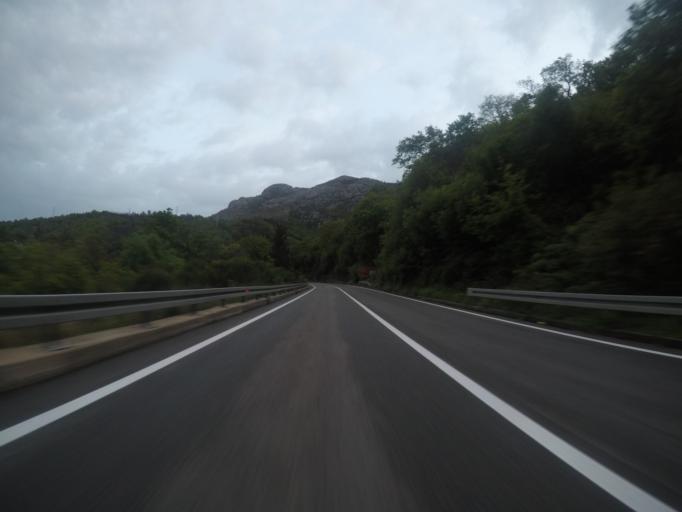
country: ME
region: Bar
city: Sutomore
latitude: 42.1718
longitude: 19.0086
